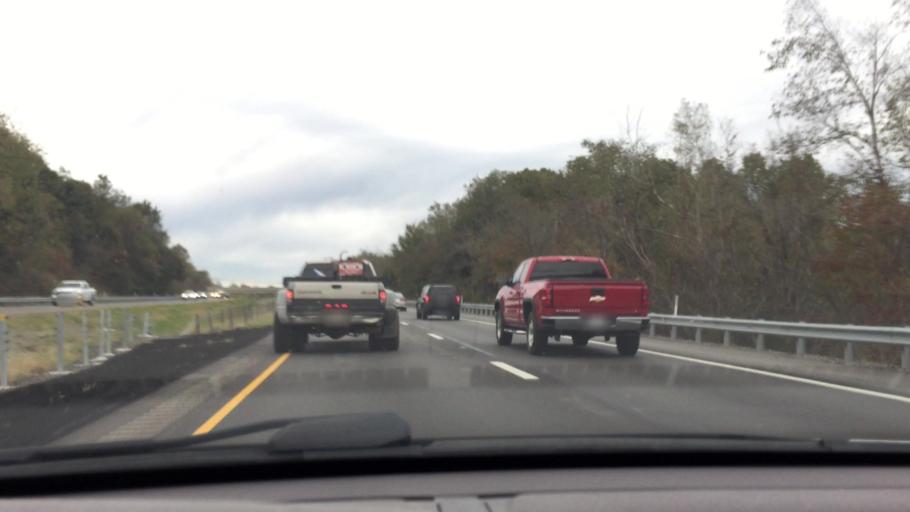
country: US
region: Pennsylvania
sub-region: Allegheny County
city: Carnot-Moon
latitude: 40.5465
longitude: -80.2736
